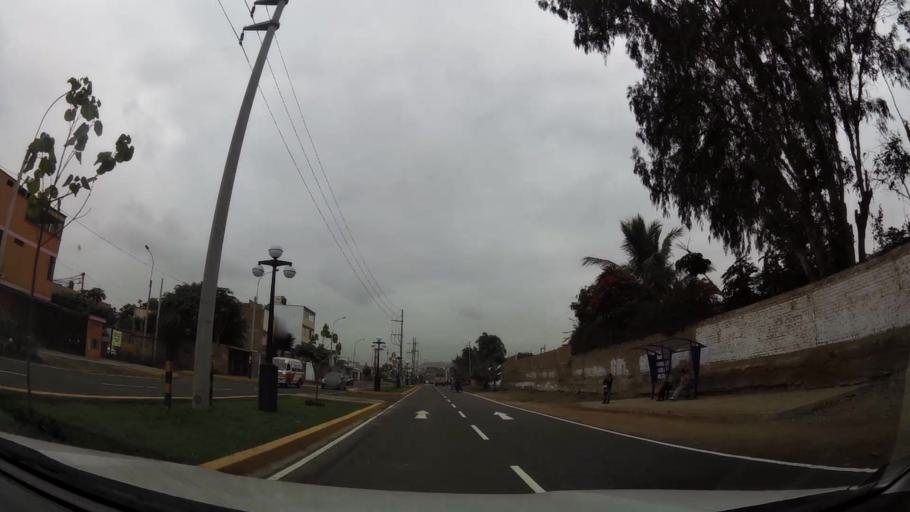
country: PE
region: Lima
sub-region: Lima
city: Surco
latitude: -12.2075
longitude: -77.0118
